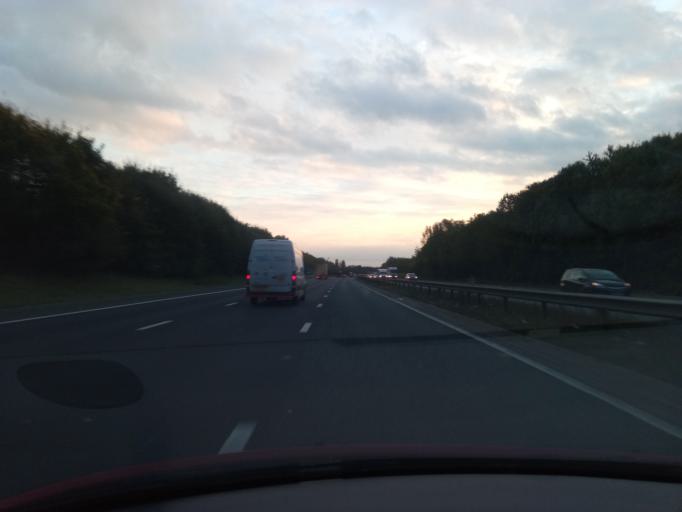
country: GB
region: England
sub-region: City and Borough of Leeds
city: Wetherby
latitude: 53.9857
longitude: -1.3628
